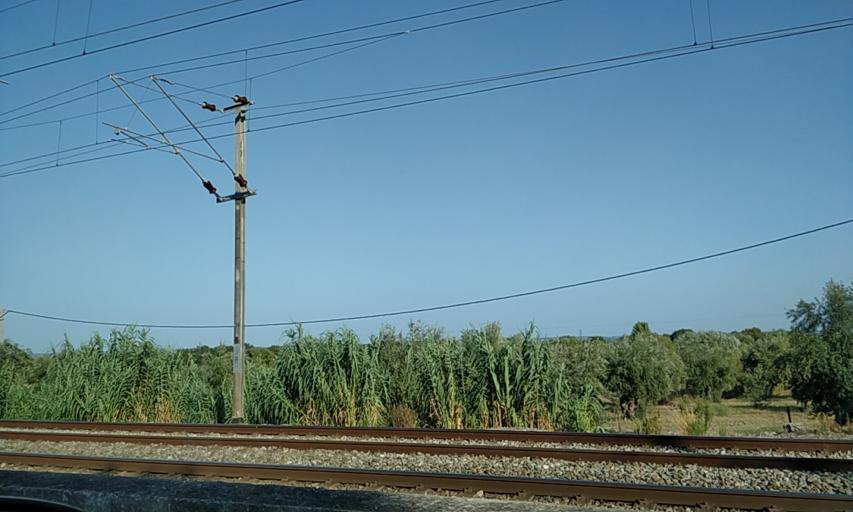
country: PT
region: Santarem
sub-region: Santarem
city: Santarem
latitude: 39.2620
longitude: -8.6664
